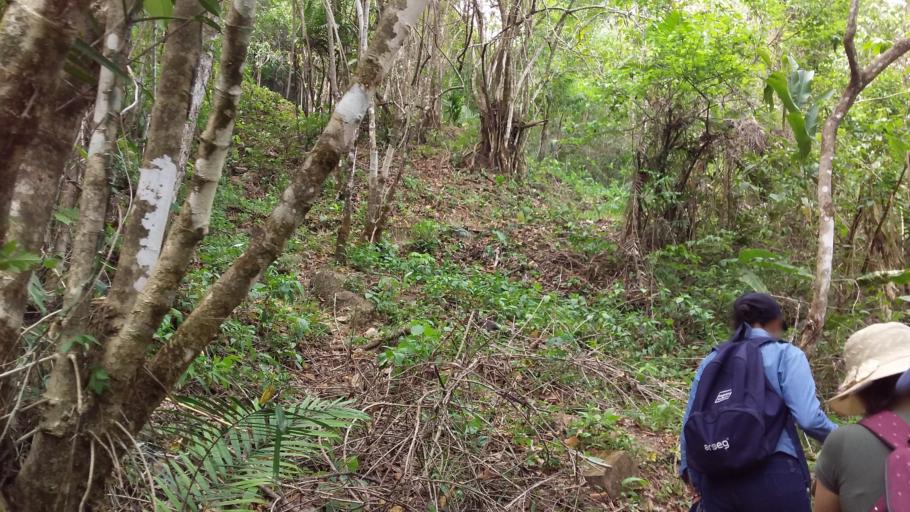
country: CO
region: Casanare
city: Nunchia
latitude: 5.6118
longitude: -72.2943
